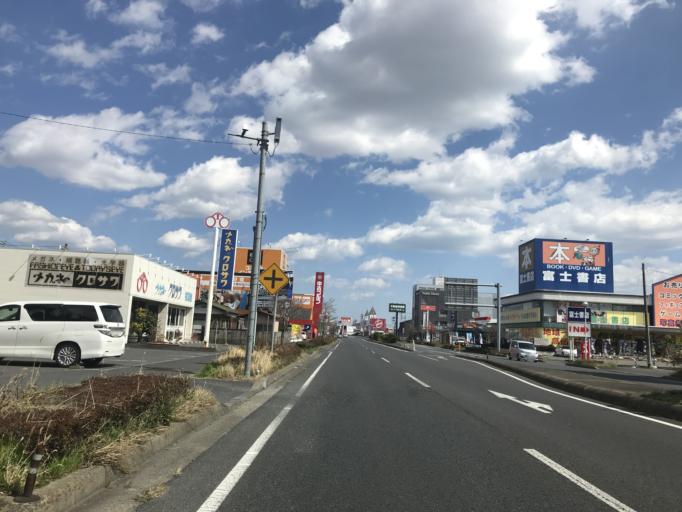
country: JP
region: Ibaraki
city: Mito-shi
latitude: 36.3480
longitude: 140.4518
